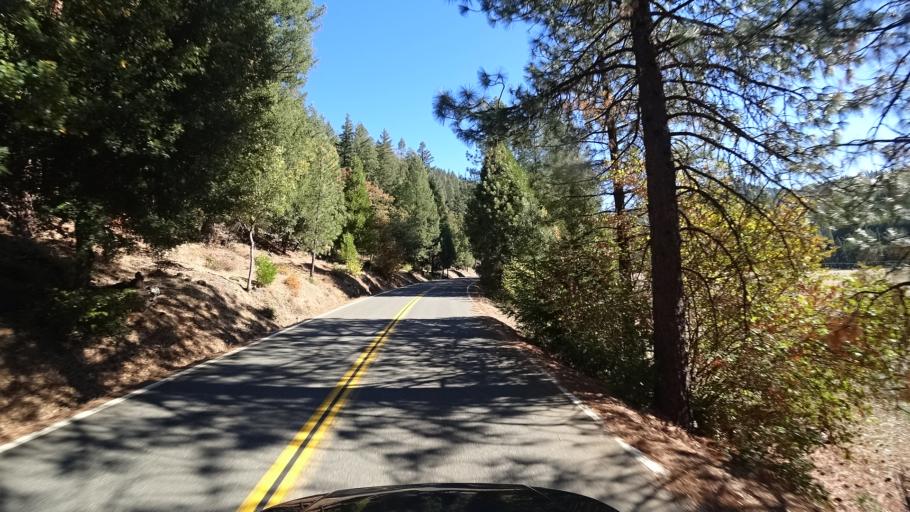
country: US
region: California
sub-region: Trinity County
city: Weaverville
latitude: 41.1407
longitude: -123.1376
